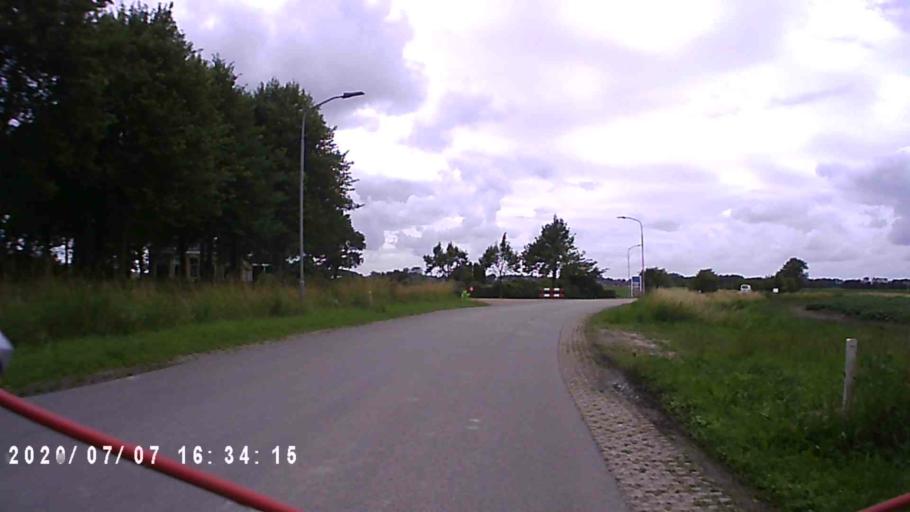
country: NL
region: Groningen
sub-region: Gemeente Winsum
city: Winsum
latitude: 53.3580
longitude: 6.5334
